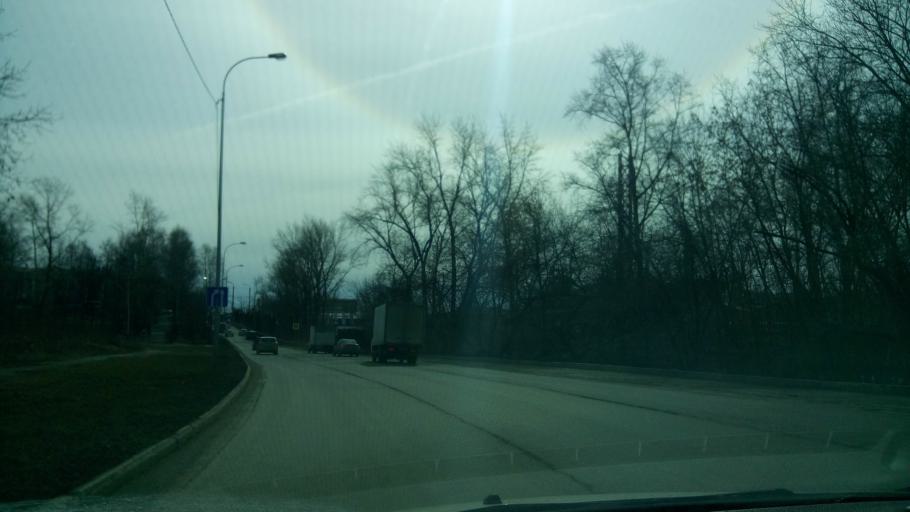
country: RU
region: Sverdlovsk
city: Nizhniy Tagil
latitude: 57.9076
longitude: 59.9463
